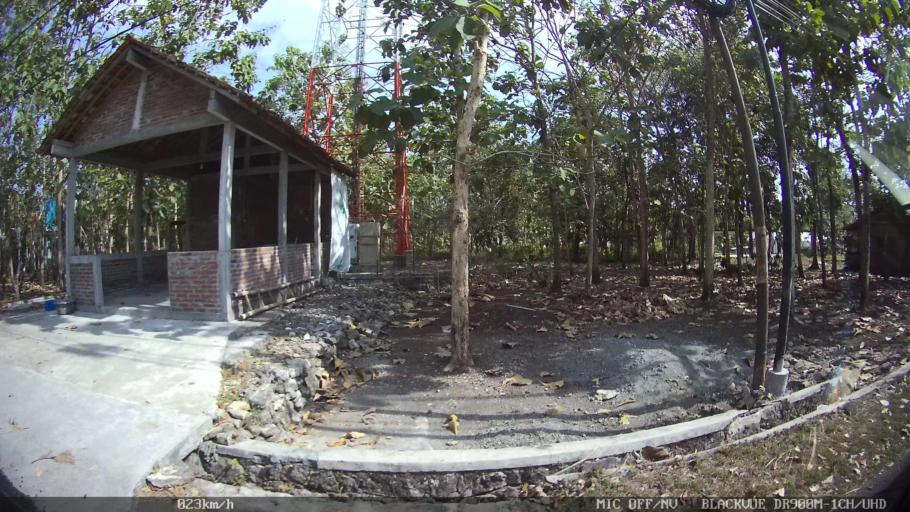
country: ID
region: Daerah Istimewa Yogyakarta
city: Bantul
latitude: -7.8590
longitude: 110.3008
